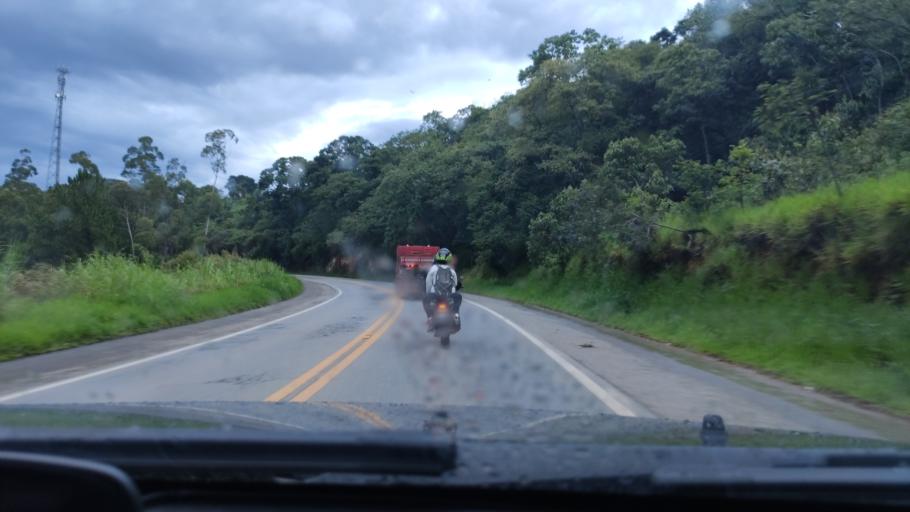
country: BR
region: Sao Paulo
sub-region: Socorro
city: Socorro
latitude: -22.7545
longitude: -46.5589
